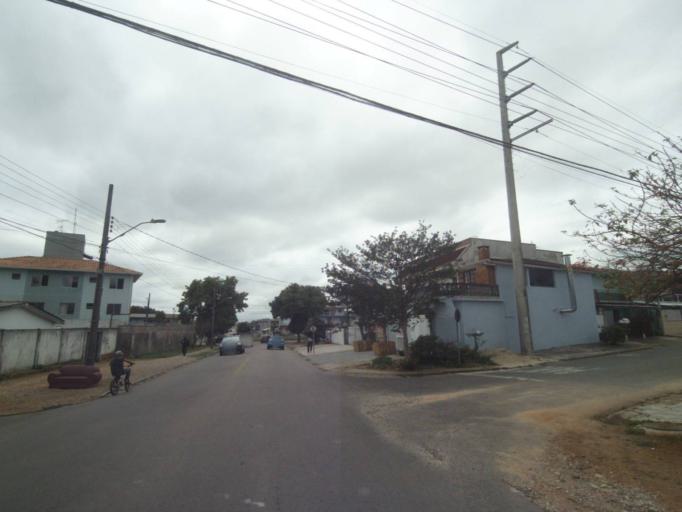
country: BR
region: Parana
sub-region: Sao Jose Dos Pinhais
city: Sao Jose dos Pinhais
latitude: -25.5449
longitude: -49.2673
